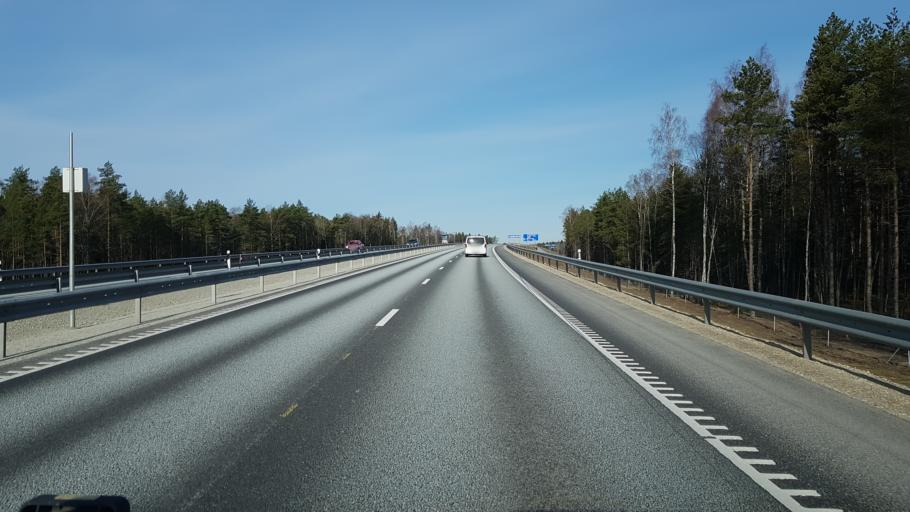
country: EE
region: Harju
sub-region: Saku vald
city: Saku
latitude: 59.3127
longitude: 24.6935
